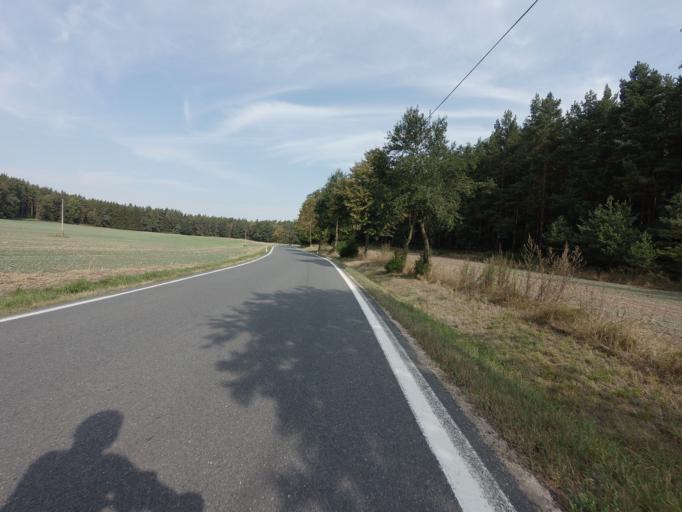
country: CZ
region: Central Bohemia
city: Petrovice
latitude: 49.5300
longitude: 14.3543
